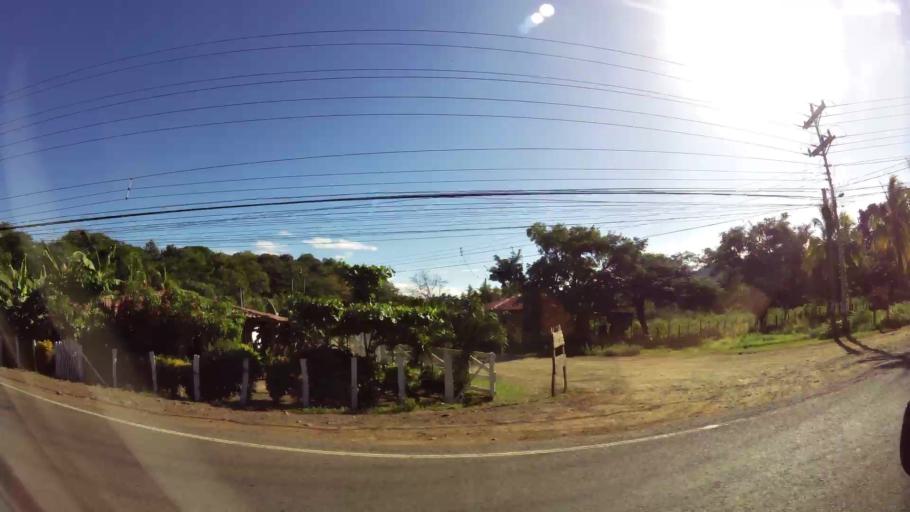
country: CR
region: Guanacaste
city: Belen
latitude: 10.3834
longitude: -85.6197
